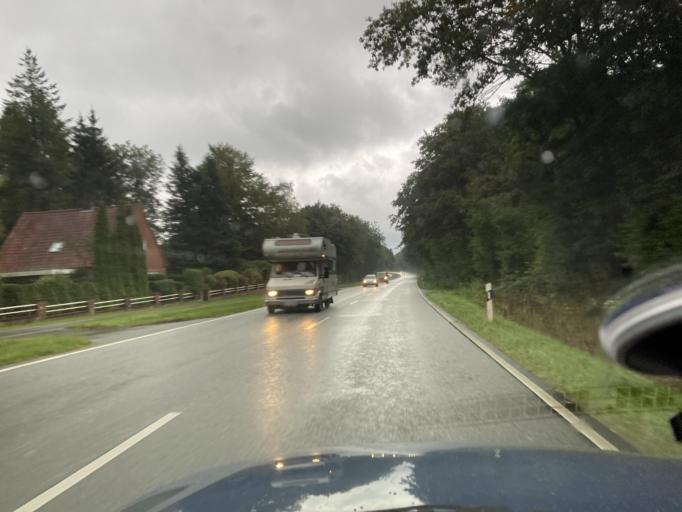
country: DE
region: Schleswig-Holstein
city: Welmbuttel
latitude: 54.2043
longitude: 9.2565
